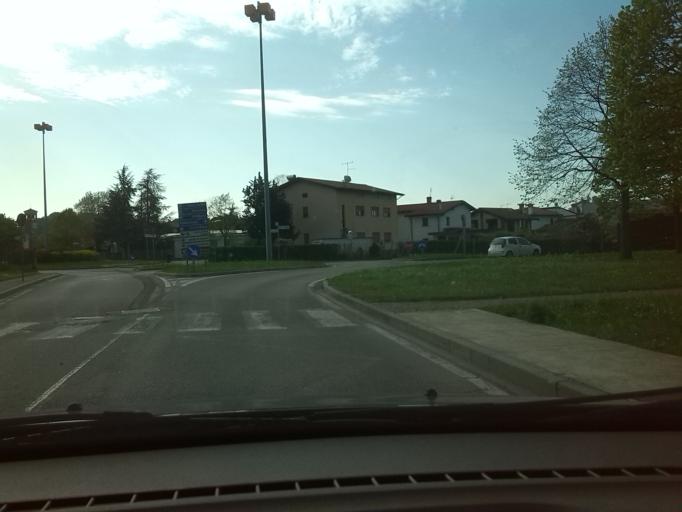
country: IT
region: Friuli Venezia Giulia
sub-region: Provincia di Udine
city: Cividale del Friuli
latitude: 46.0860
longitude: 13.4303
